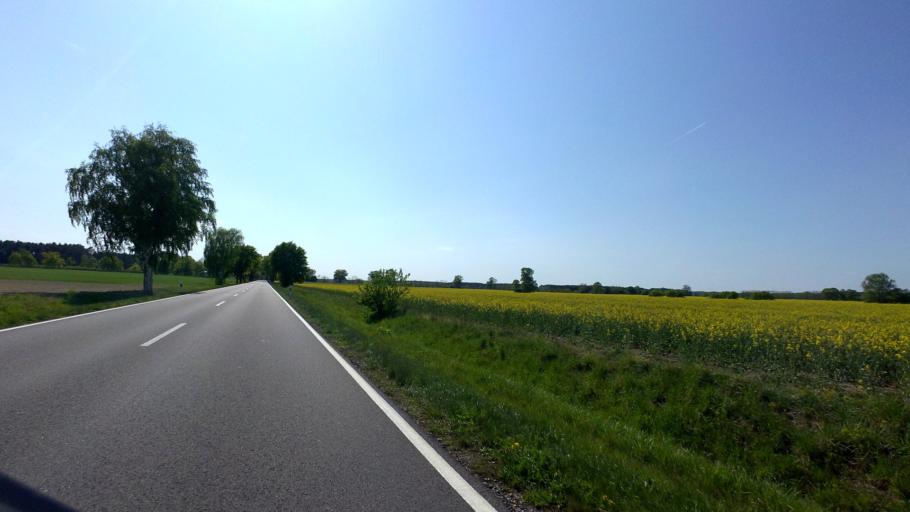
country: DE
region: Brandenburg
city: Neu Zauche
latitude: 52.0184
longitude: 14.0725
